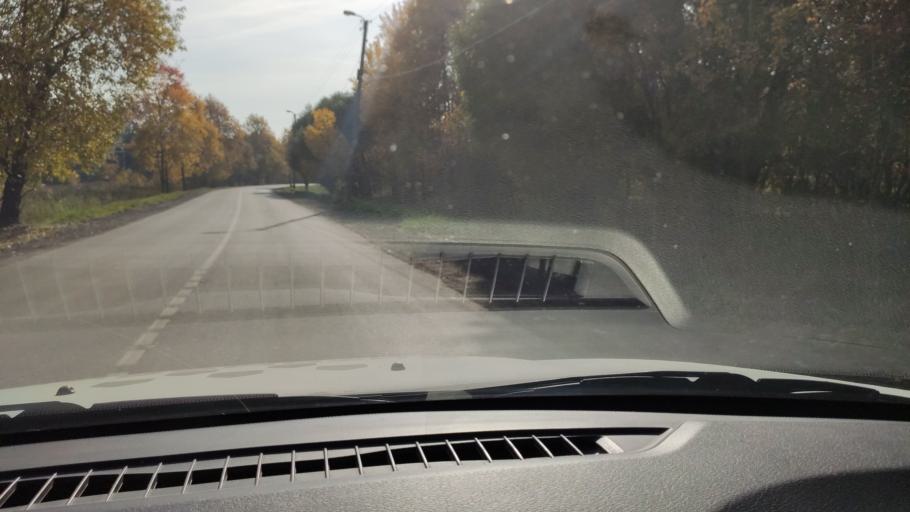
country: RU
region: Perm
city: Sylva
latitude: 58.0331
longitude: 56.7398
